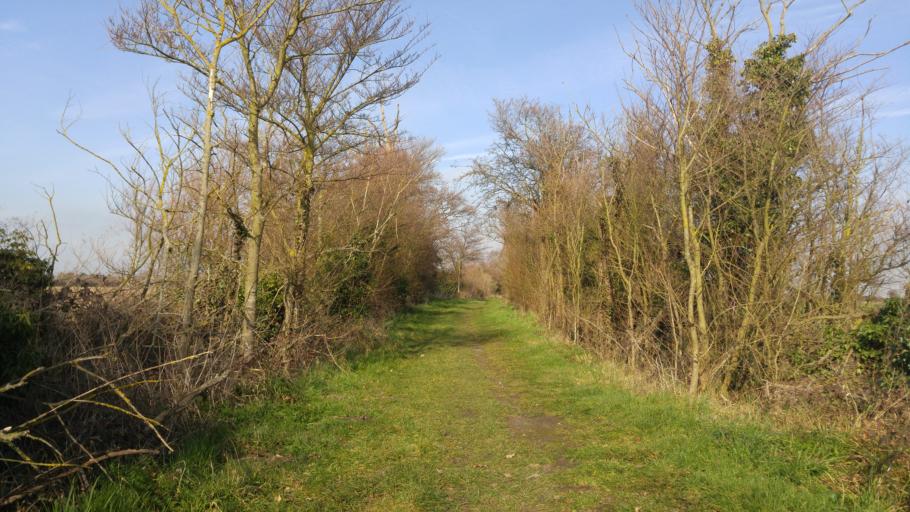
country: GB
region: England
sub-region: Essex
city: Little Clacton
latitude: 51.8205
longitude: 1.1706
